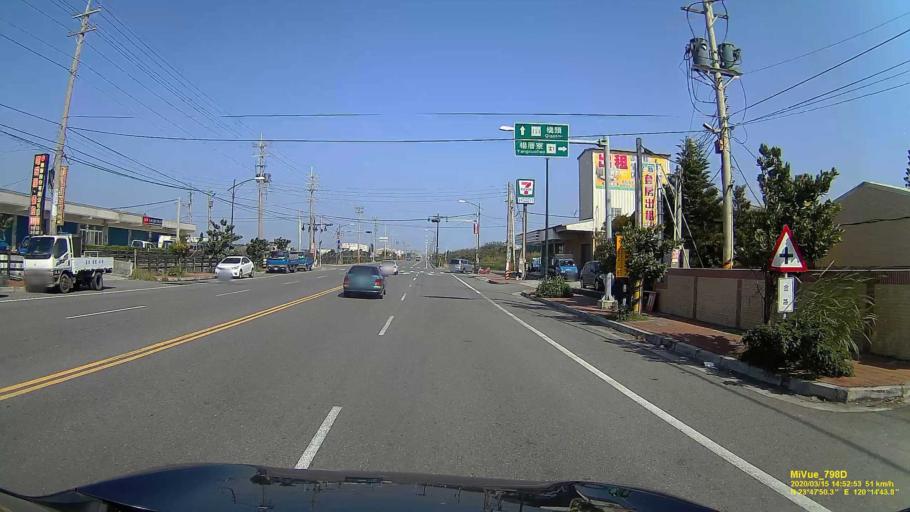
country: TW
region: Taiwan
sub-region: Yunlin
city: Douliu
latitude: 23.7973
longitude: 120.2458
